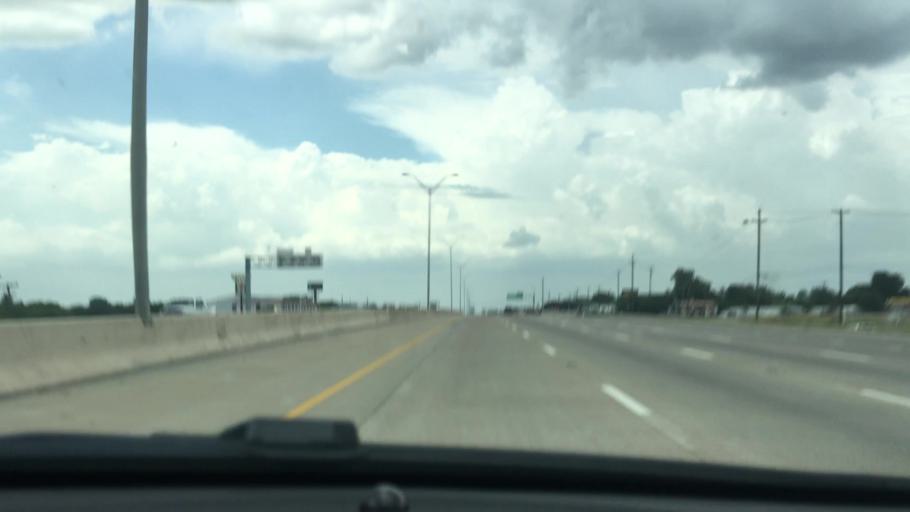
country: US
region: Texas
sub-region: Dallas County
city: DeSoto
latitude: 32.6168
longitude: -96.8230
